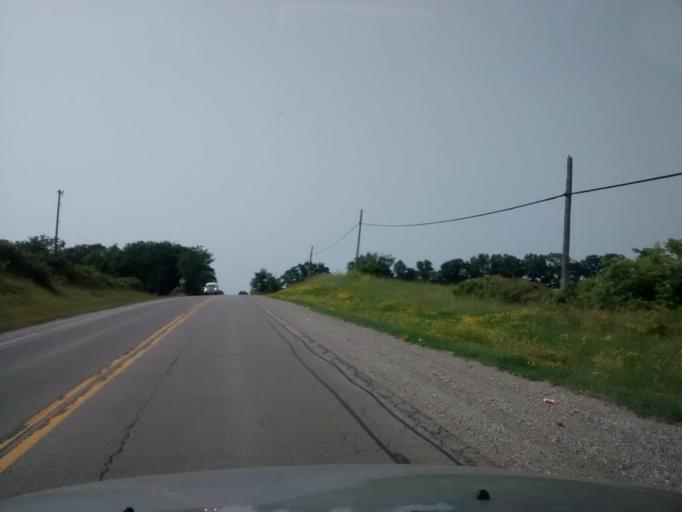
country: CA
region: Ontario
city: Ancaster
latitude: 42.9711
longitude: -79.8690
